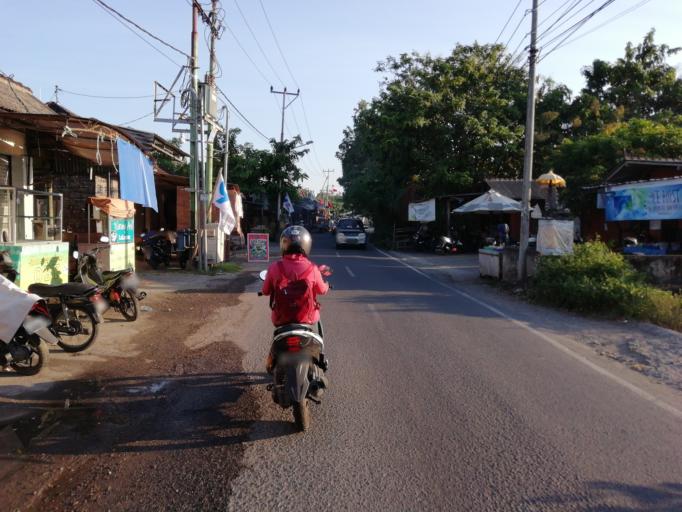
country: ID
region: Bali
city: Bualu
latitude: -8.7914
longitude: 115.1961
